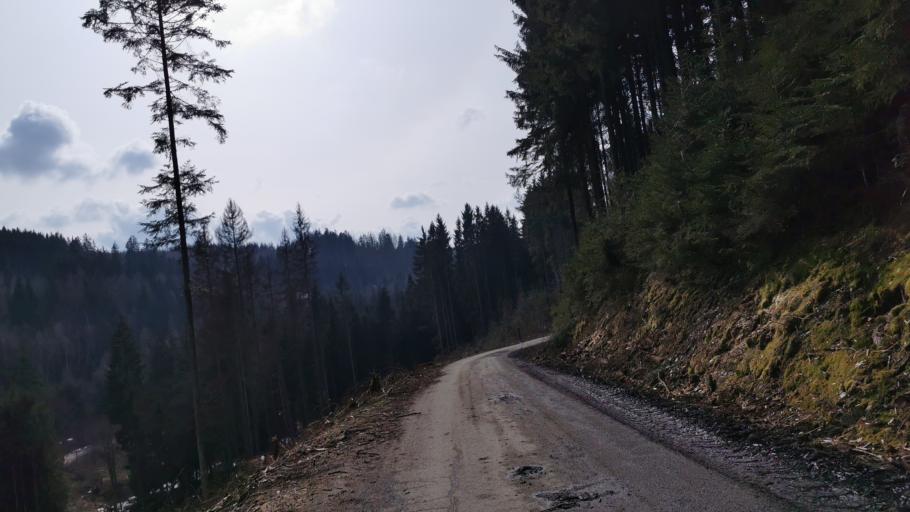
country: DE
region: Bavaria
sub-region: Upper Franconia
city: Ludwigsstadt
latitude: 50.4774
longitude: 11.4190
